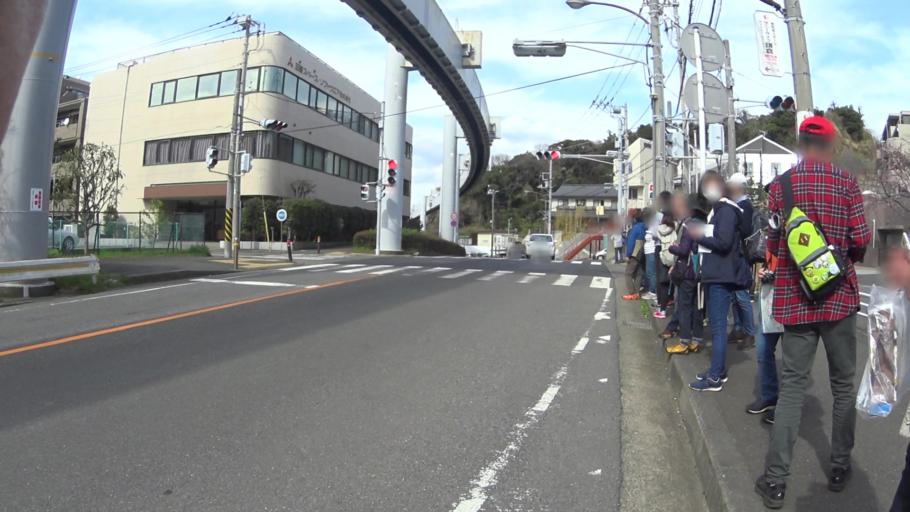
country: JP
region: Kanagawa
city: Kamakura
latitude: 35.3358
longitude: 139.5222
